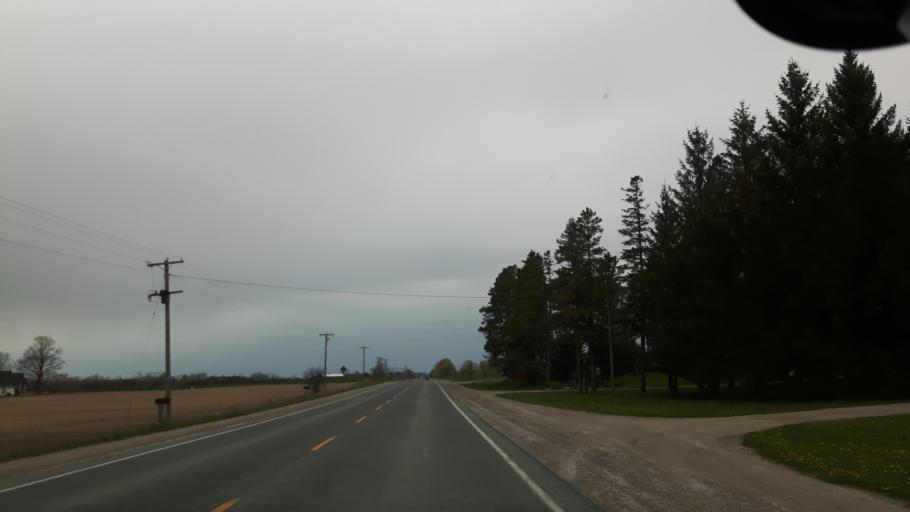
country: CA
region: Ontario
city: Bluewater
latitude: 43.6270
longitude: -81.5624
